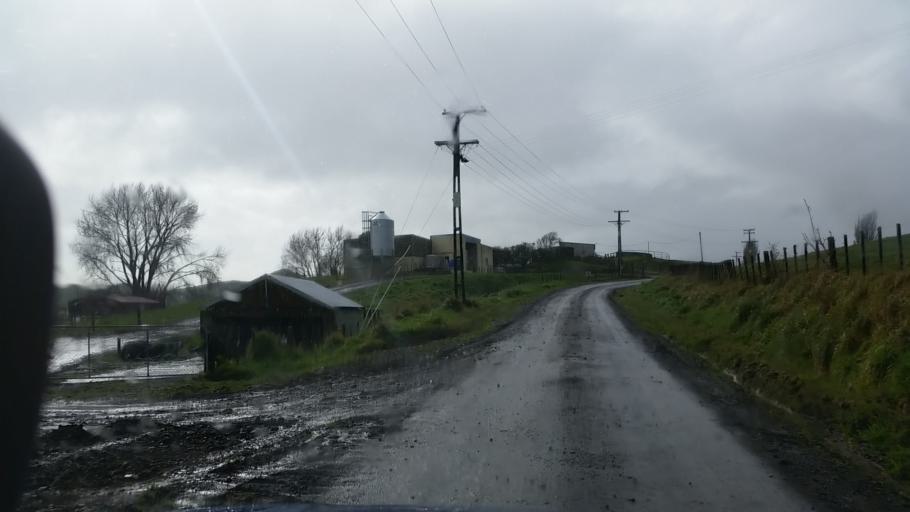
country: NZ
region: Taranaki
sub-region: South Taranaki District
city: Eltham
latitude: -39.3522
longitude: 174.4352
